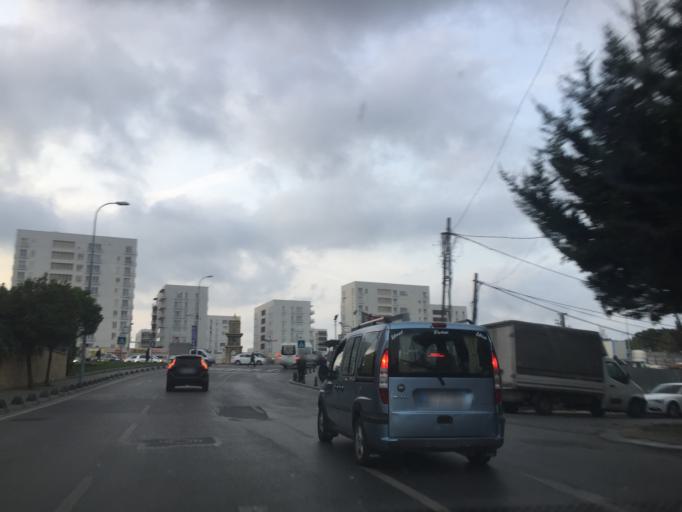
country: TR
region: Istanbul
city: Samandira
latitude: 40.9897
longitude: 29.2298
